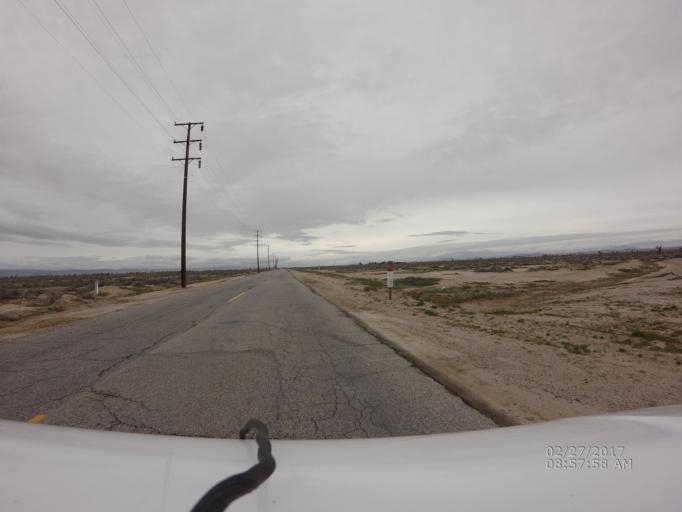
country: US
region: California
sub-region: Los Angeles County
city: Lancaster
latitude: 34.7631
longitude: -118.0543
